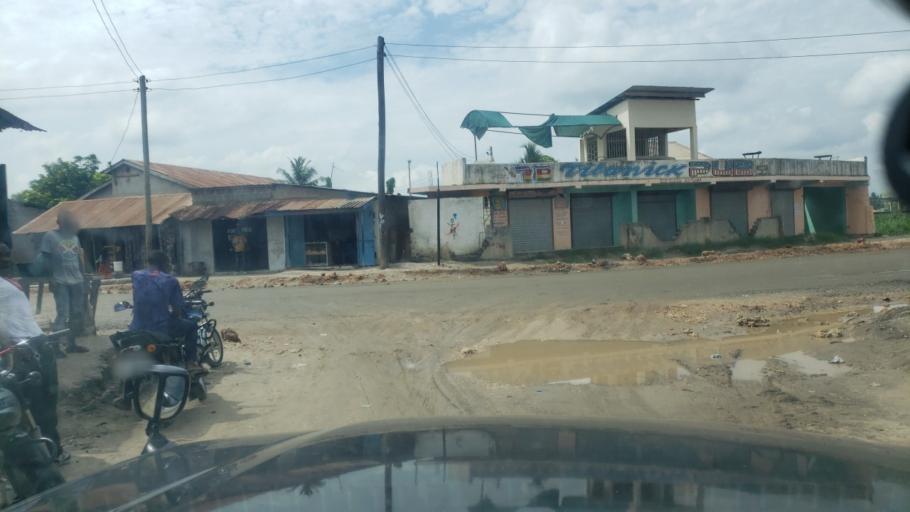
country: TZ
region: Pwani
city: Vikindu
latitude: -6.9270
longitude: 39.2547
